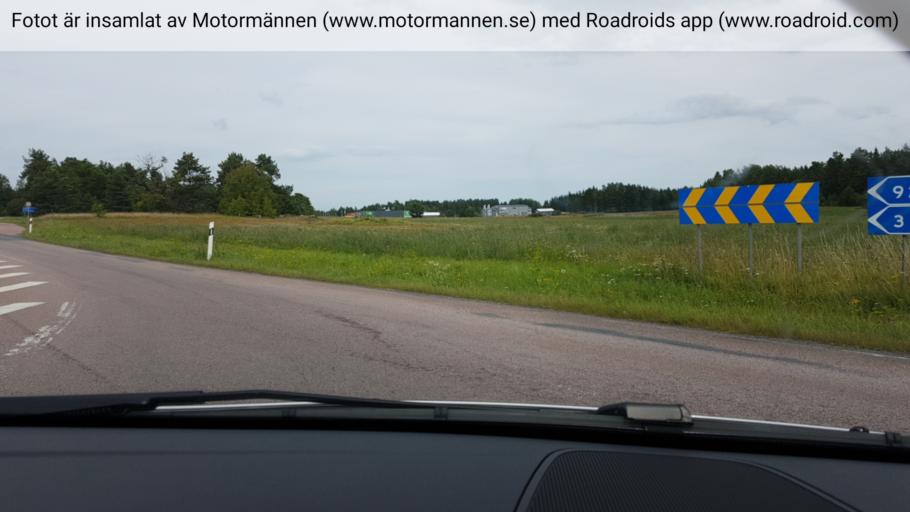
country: SE
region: Uppsala
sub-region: Osthammars Kommun
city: OEsthammar
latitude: 60.2434
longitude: 18.3488
